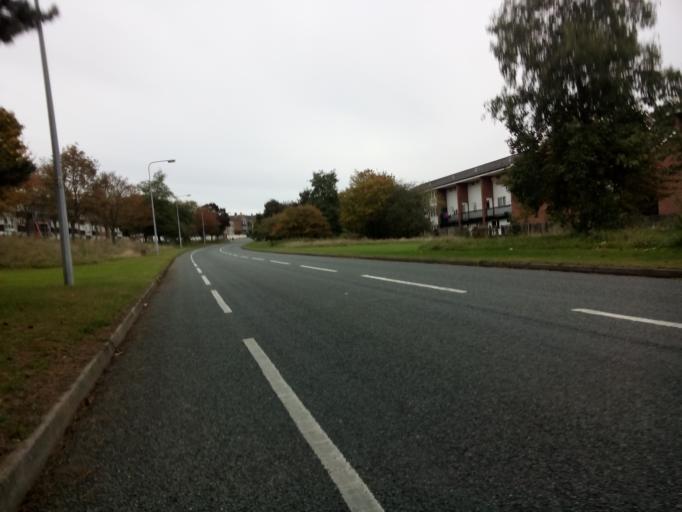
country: GB
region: England
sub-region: Suffolk
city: Ipswich
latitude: 52.0397
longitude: 1.1239
